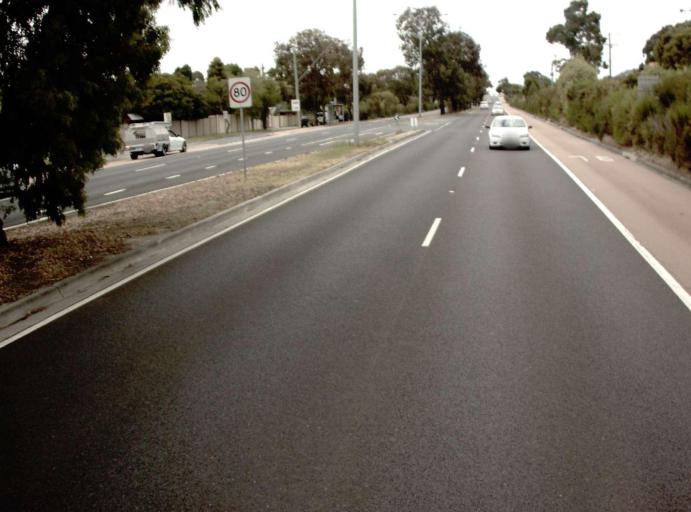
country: AU
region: Victoria
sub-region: Knox
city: Scoresby
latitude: -37.8941
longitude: 145.2330
